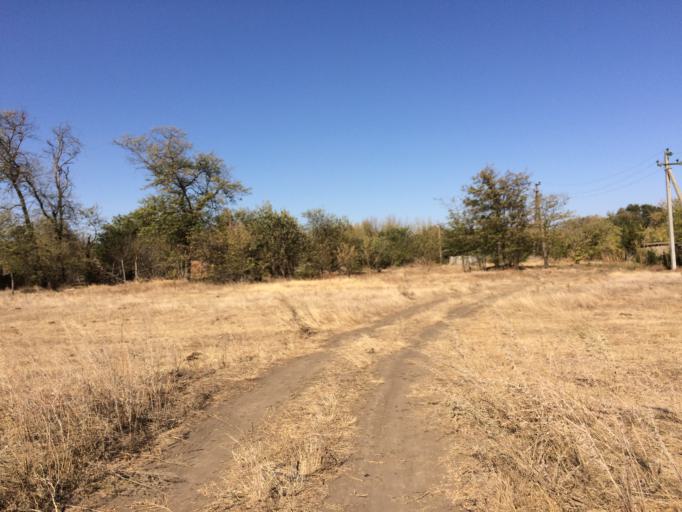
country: RU
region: Rostov
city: Tselina
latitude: 46.5132
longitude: 41.1860
